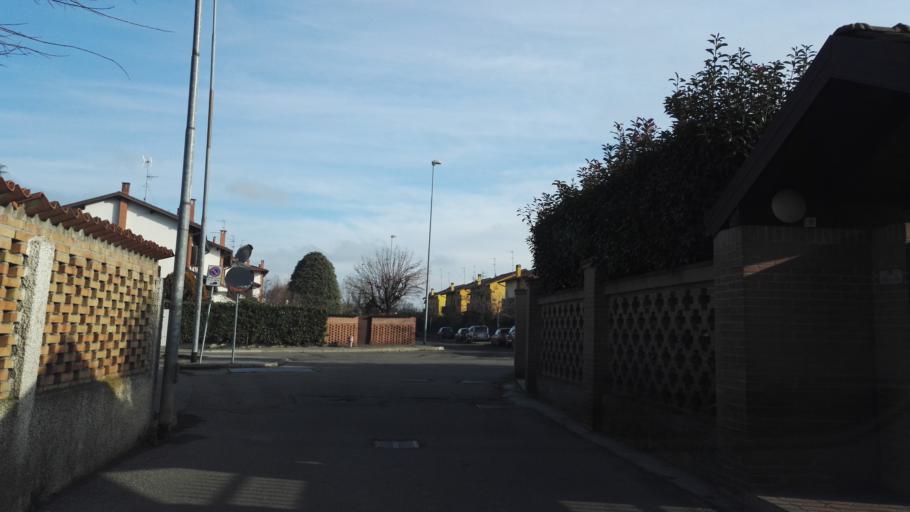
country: IT
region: Lombardy
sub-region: Citta metropolitana di Milano
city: Civesio
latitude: 45.3934
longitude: 9.2680
